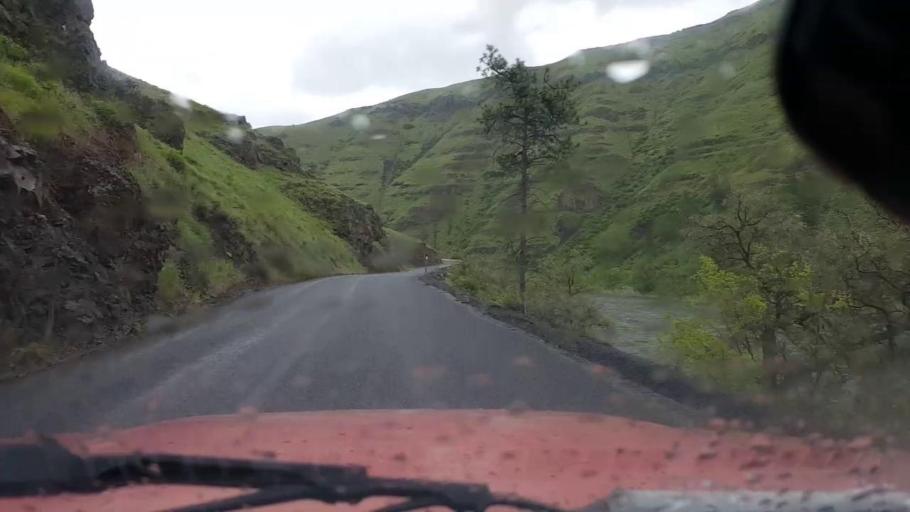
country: US
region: Washington
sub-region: Asotin County
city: Asotin
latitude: 46.0311
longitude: -117.2987
